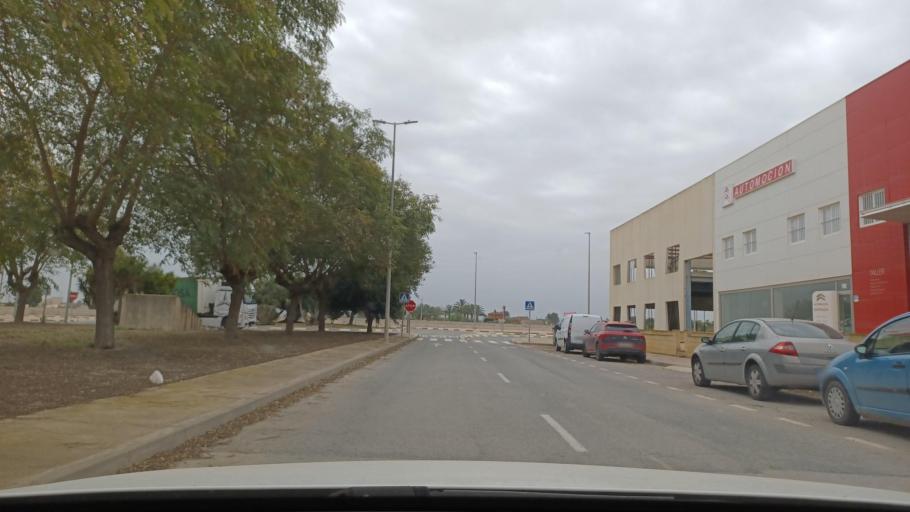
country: ES
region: Valencia
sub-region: Provincia de Alicante
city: Dolores
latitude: 38.1429
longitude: -0.7414
